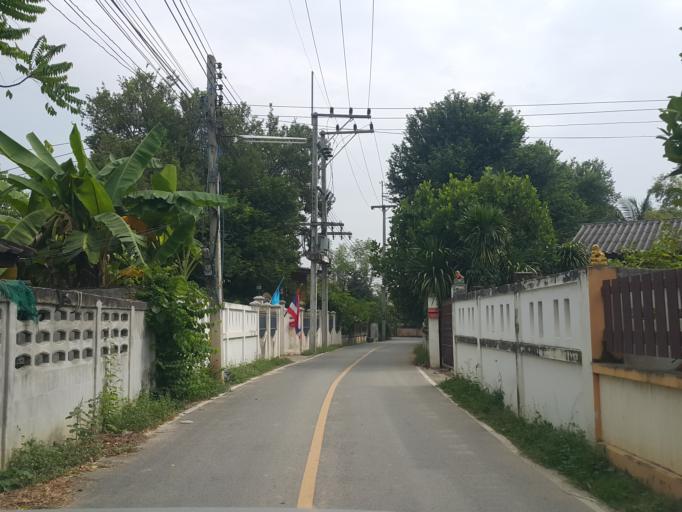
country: TH
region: Chiang Mai
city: San Sai
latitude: 18.8019
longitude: 99.0744
